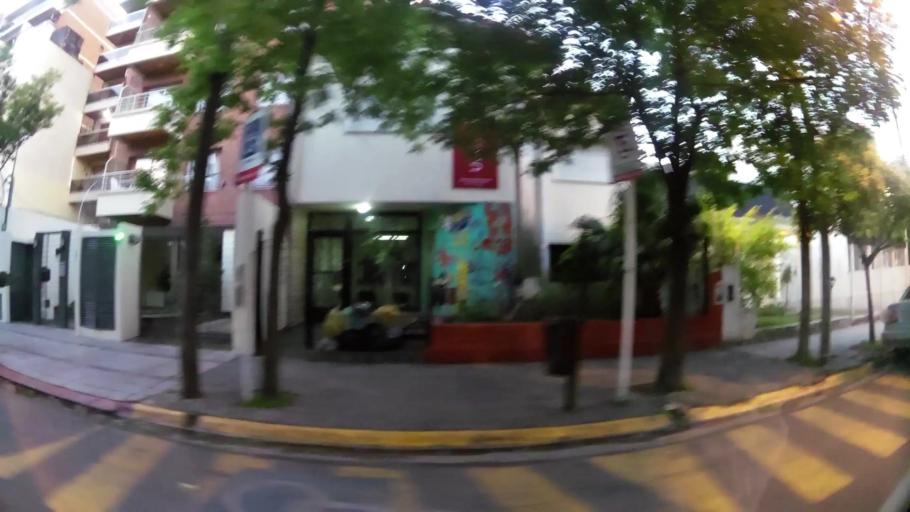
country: AR
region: Buenos Aires
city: Ituzaingo
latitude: -34.6533
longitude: -58.6412
